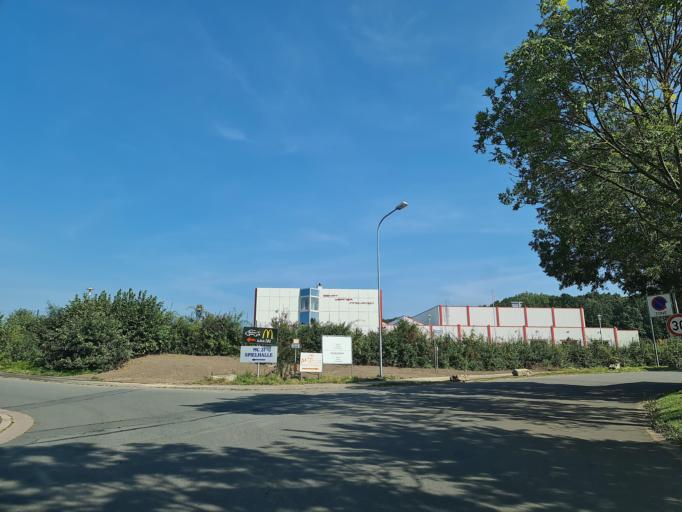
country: DE
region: Thuringia
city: Petersberg
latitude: 50.9686
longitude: 11.8544
